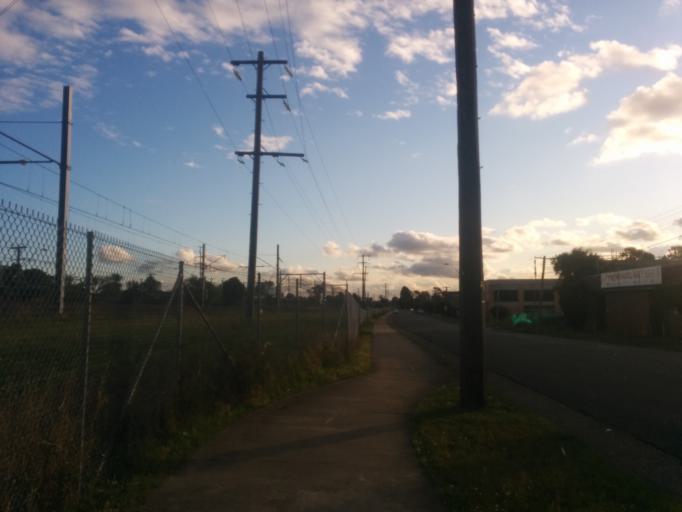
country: AU
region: New South Wales
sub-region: Holroyd
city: Guildford West
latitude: -33.8599
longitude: 150.9795
